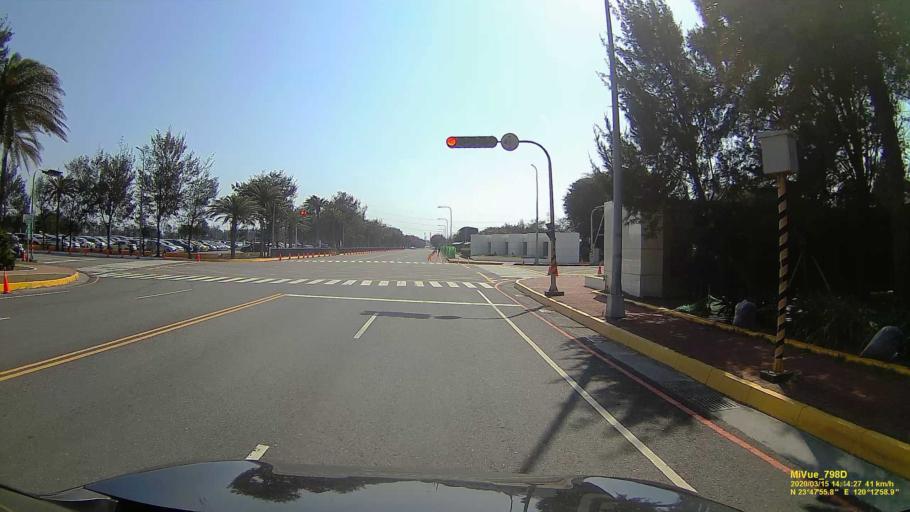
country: TW
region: Taiwan
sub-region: Yunlin
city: Douliu
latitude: 23.7987
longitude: 120.2162
